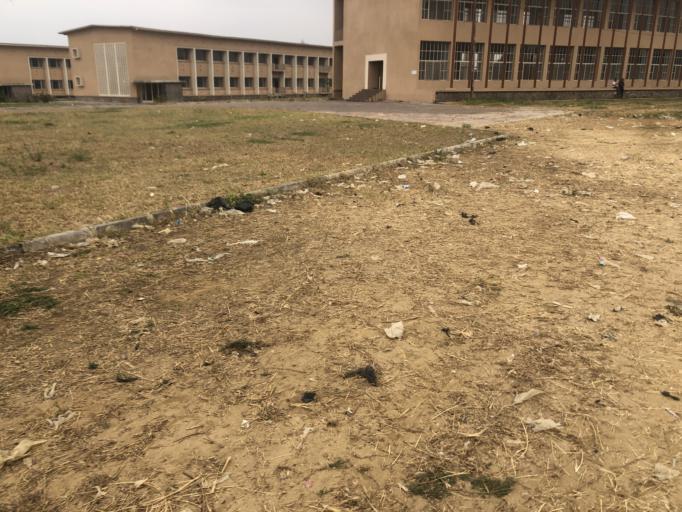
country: CD
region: Kinshasa
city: Masina
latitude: -4.4253
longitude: 15.3097
